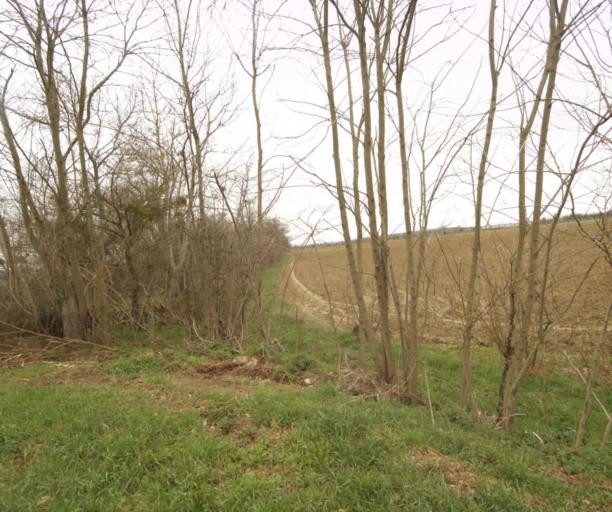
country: FR
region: Midi-Pyrenees
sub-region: Departement de l'Ariege
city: Pamiers
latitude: 43.1576
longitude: 1.6283
